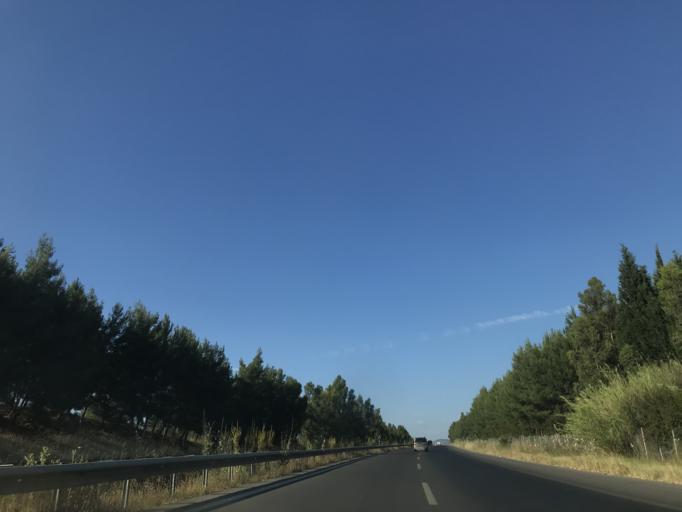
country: TR
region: Aydin
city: Ortaklar
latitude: 37.8492
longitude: 27.5463
